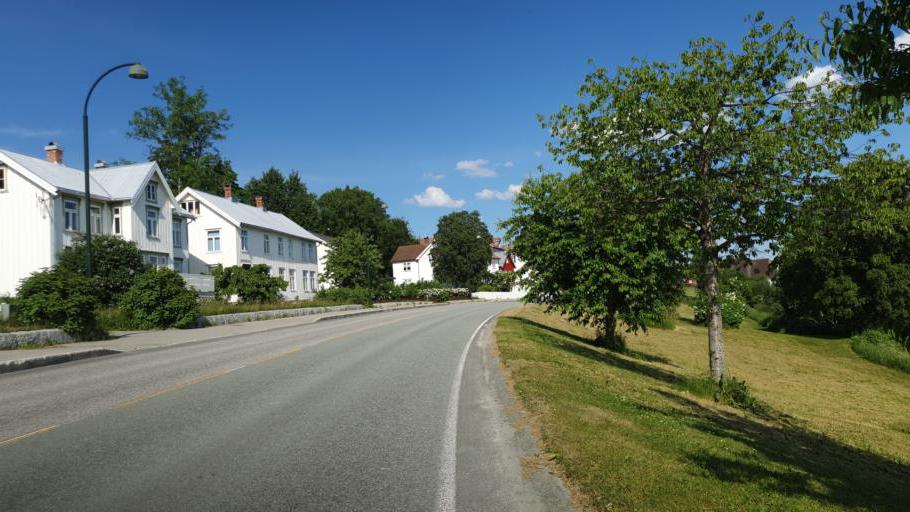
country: NO
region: Nord-Trondelag
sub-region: Leksvik
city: Leksvik
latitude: 63.6715
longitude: 10.6219
